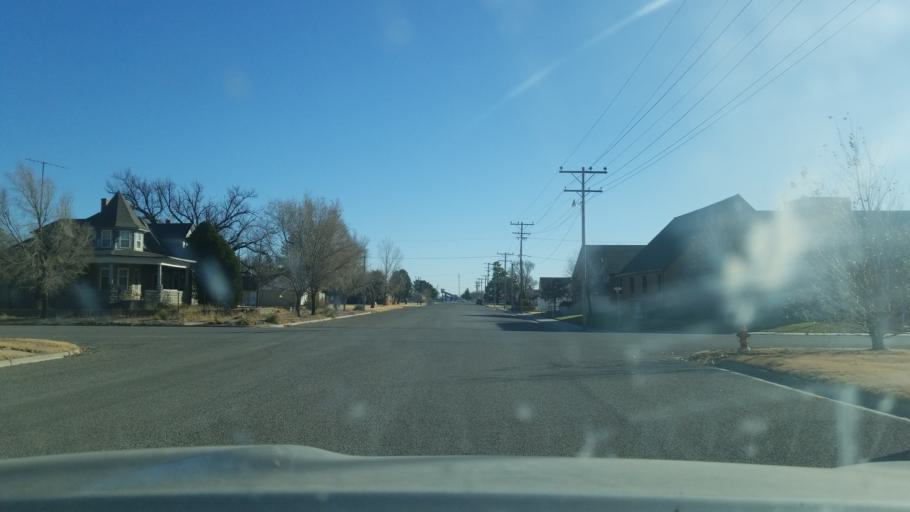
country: US
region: Kansas
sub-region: Ness County
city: Ness City
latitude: 38.4539
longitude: -99.9027
